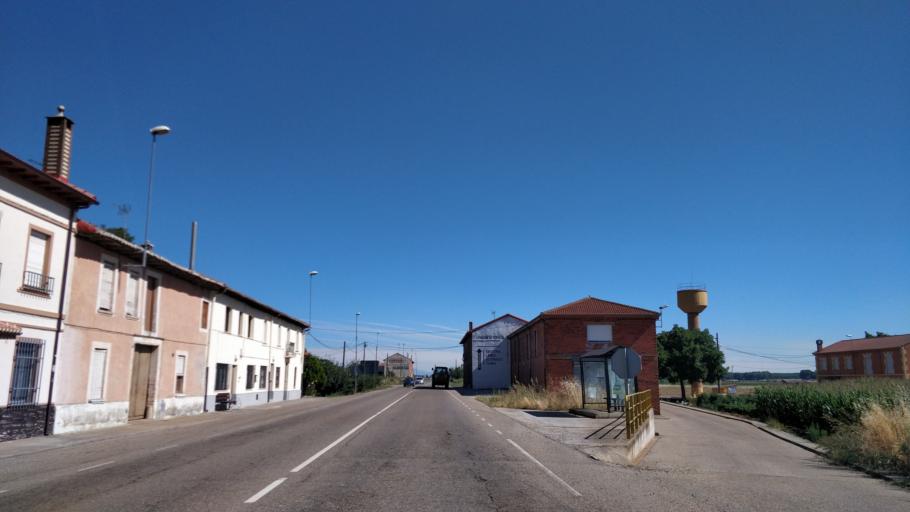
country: ES
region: Castille and Leon
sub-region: Provincia de Leon
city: San Cristobal de la Polantera
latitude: 42.3768
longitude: -5.8890
